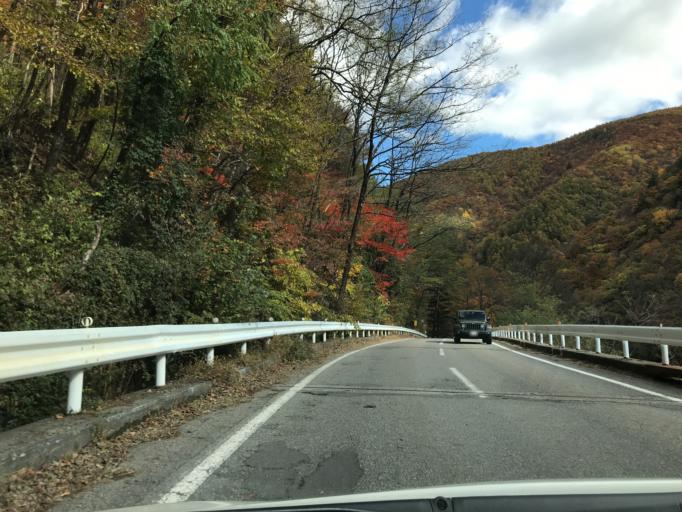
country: JP
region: Nagano
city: Toyoshina
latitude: 36.1301
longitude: 137.6691
